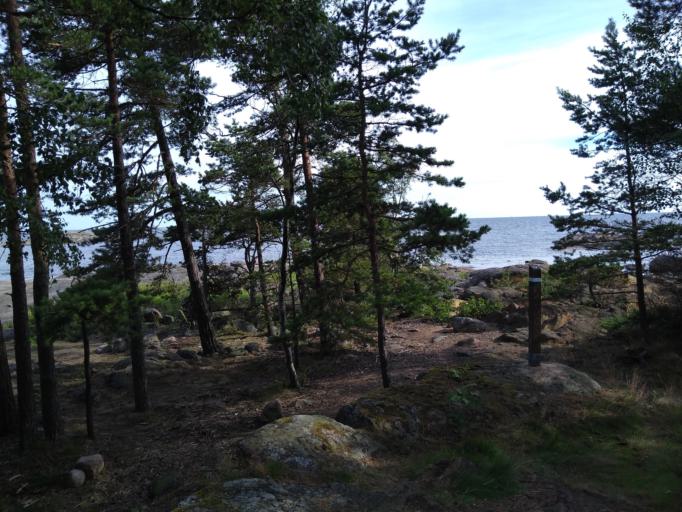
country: FI
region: Uusimaa
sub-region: Helsinki
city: Helsinki
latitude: 60.1363
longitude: 24.9166
